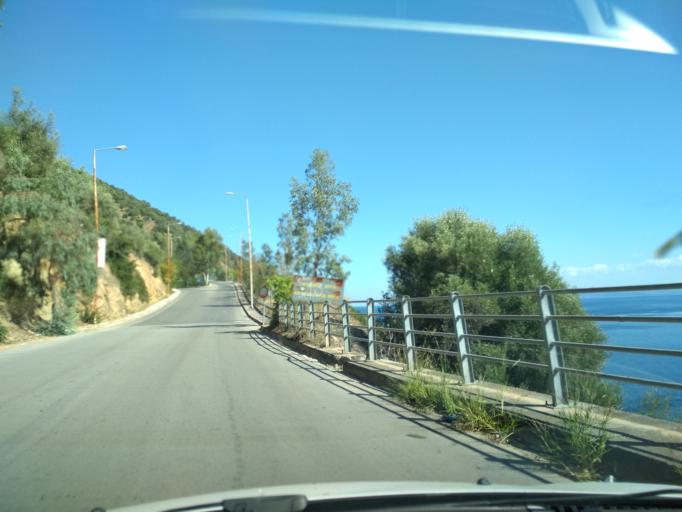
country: GR
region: Central Greece
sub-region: Nomos Evvoias
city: Oreoi
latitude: 38.8528
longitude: 23.0533
